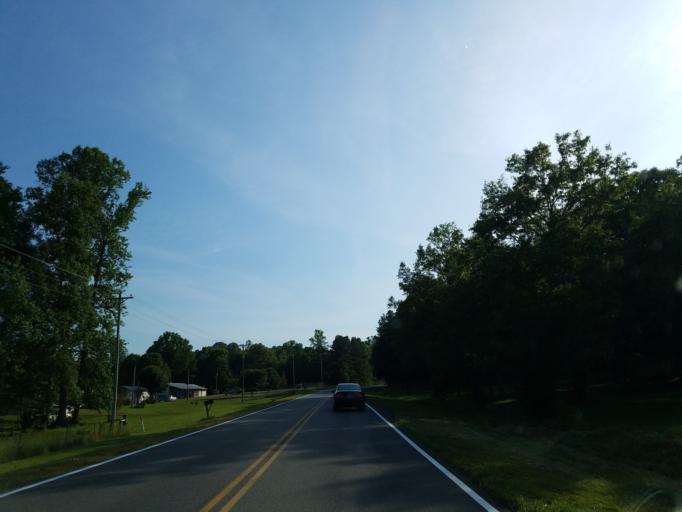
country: US
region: Georgia
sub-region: Chattooga County
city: Trion
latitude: 34.5531
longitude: -85.1928
